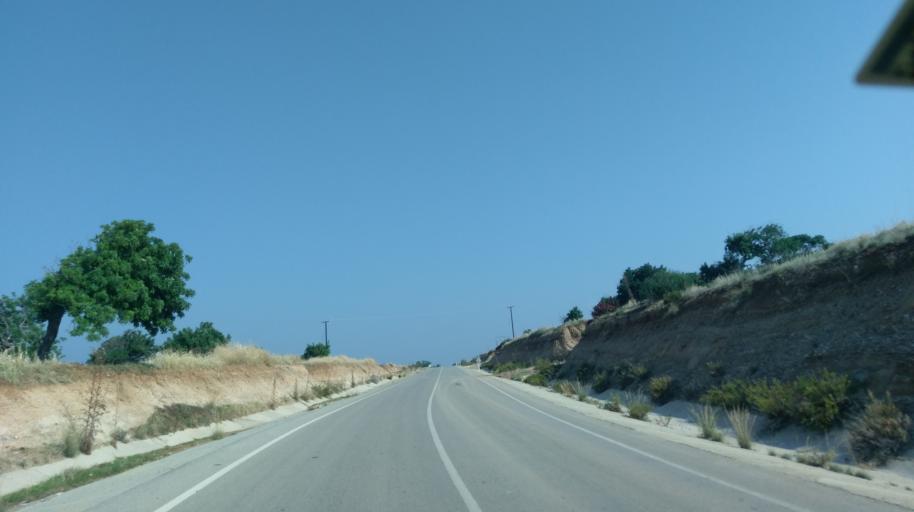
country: CY
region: Ammochostos
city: Lefkonoiko
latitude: 35.3833
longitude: 33.7210
